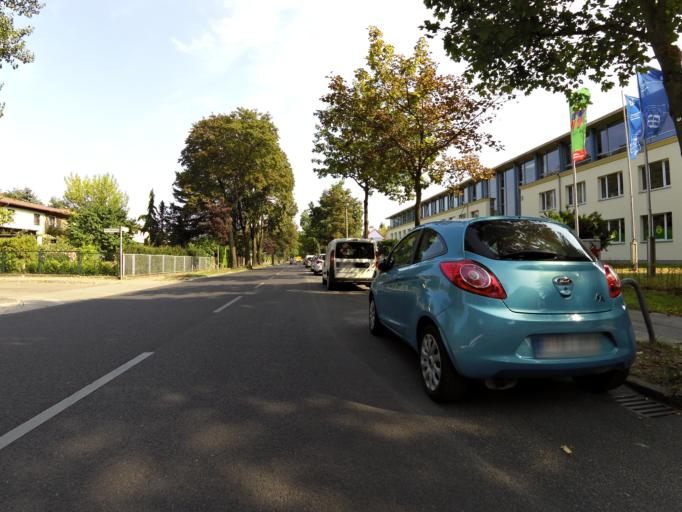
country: DE
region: Berlin
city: Grunau
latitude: 52.4123
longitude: 13.5667
